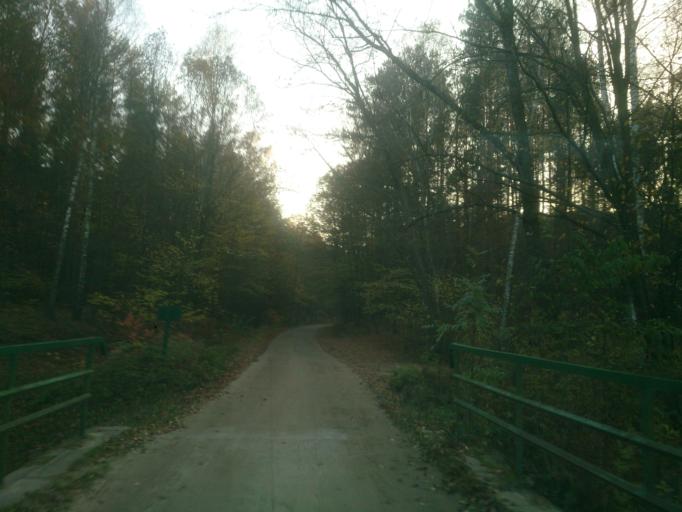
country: PL
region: Kujawsko-Pomorskie
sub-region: Powiat brodnicki
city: Brodnica
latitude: 53.3476
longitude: 19.4272
